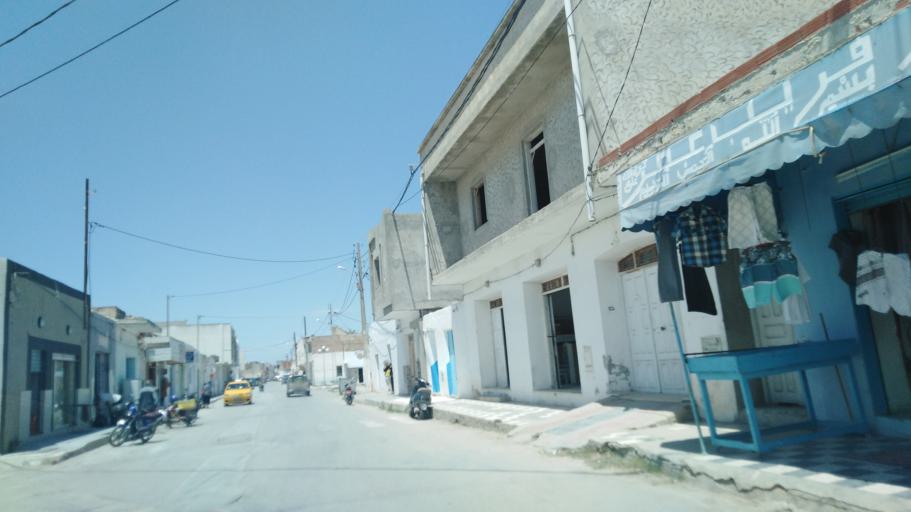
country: TN
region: Al Mahdiyah
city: Ksour Essaf
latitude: 35.4171
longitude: 10.9870
